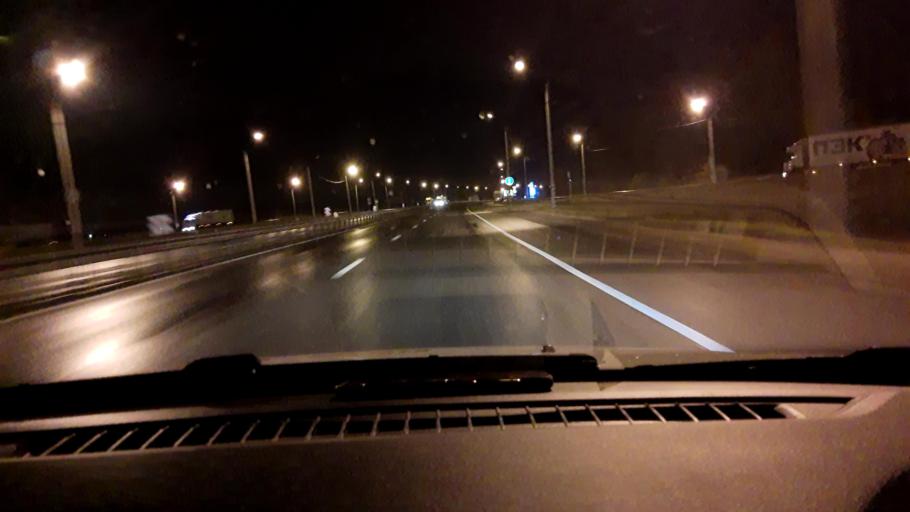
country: RU
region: Nizjnij Novgorod
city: Kstovo
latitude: 56.1269
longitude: 44.2618
